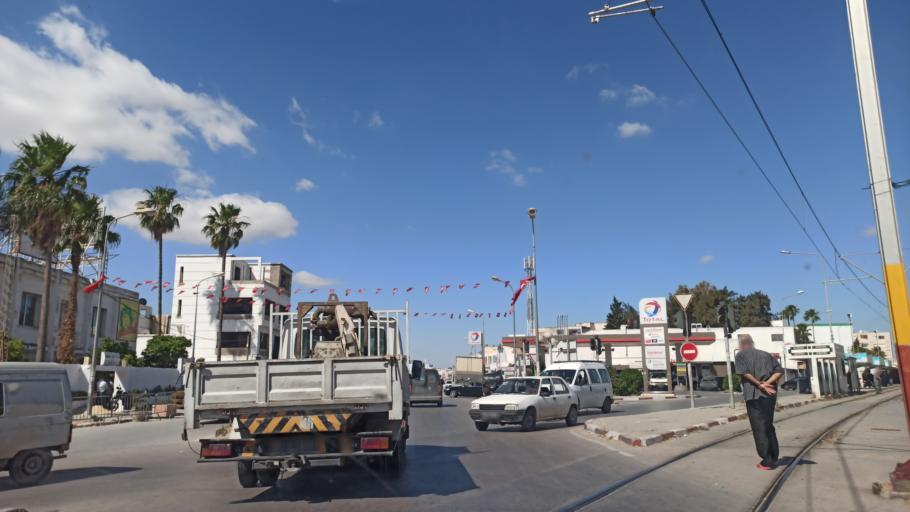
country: TN
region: Manouba
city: Manouba
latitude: 36.8022
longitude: 10.1118
